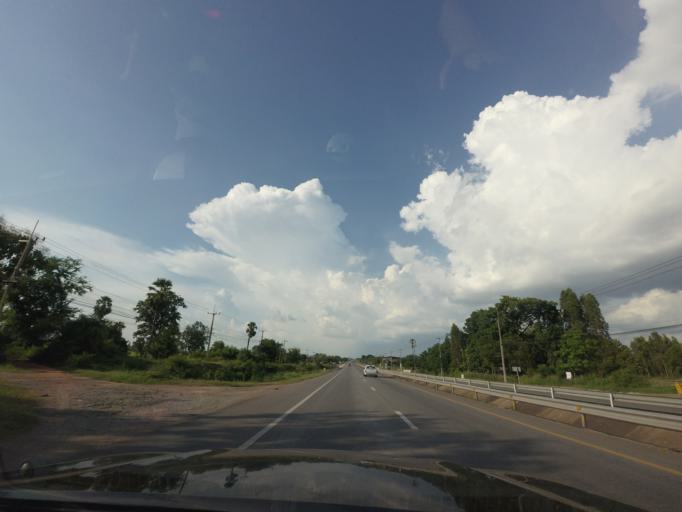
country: TH
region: Khon Kaen
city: Ban Haet
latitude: 16.1997
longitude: 102.7594
